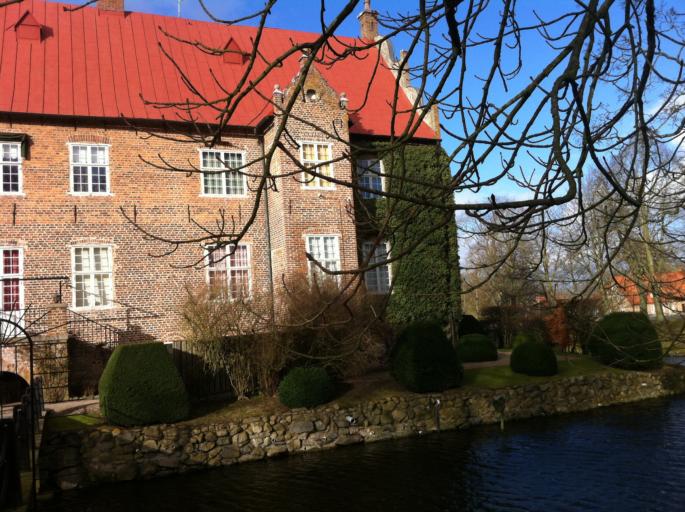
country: SE
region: Skane
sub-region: Kristianstads Kommun
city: Fjalkinge
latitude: 56.0215
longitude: 14.3702
